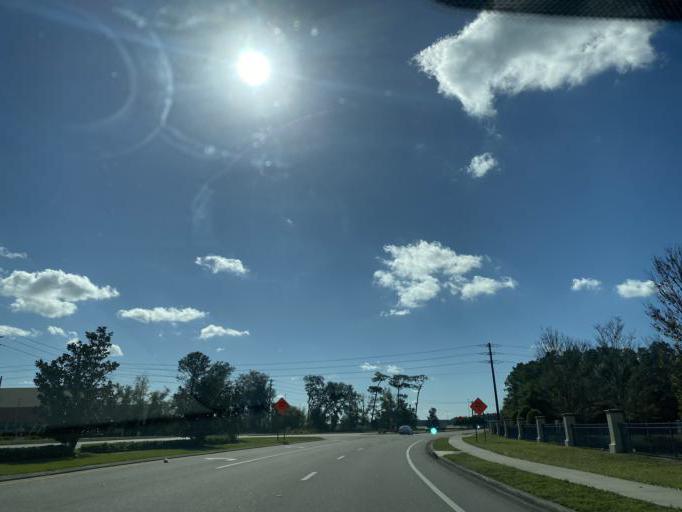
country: US
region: Florida
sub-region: Seminole County
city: Heathrow
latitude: 28.8018
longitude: -81.3481
